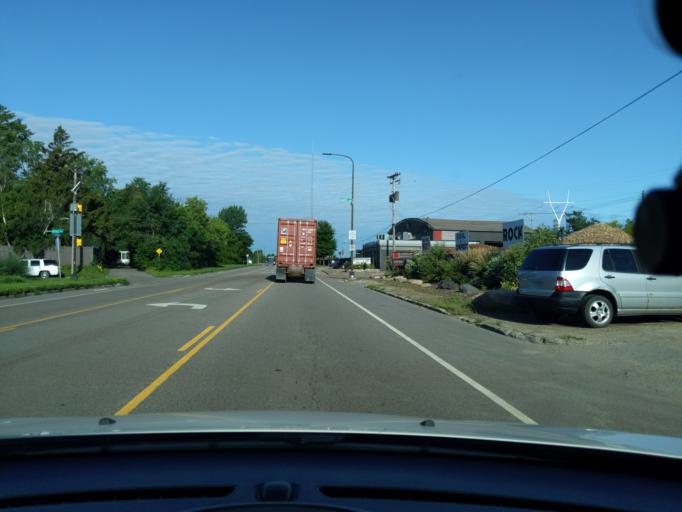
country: US
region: Minnesota
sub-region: Ramsey County
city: Falcon Heights
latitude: 44.9682
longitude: -93.1582
